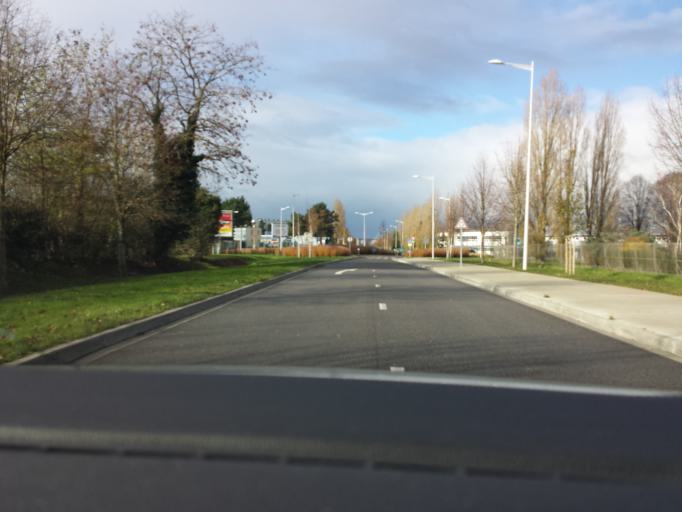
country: FR
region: Haute-Normandie
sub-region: Departement de l'Eure
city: Evreux
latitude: 49.0166
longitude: 1.1723
